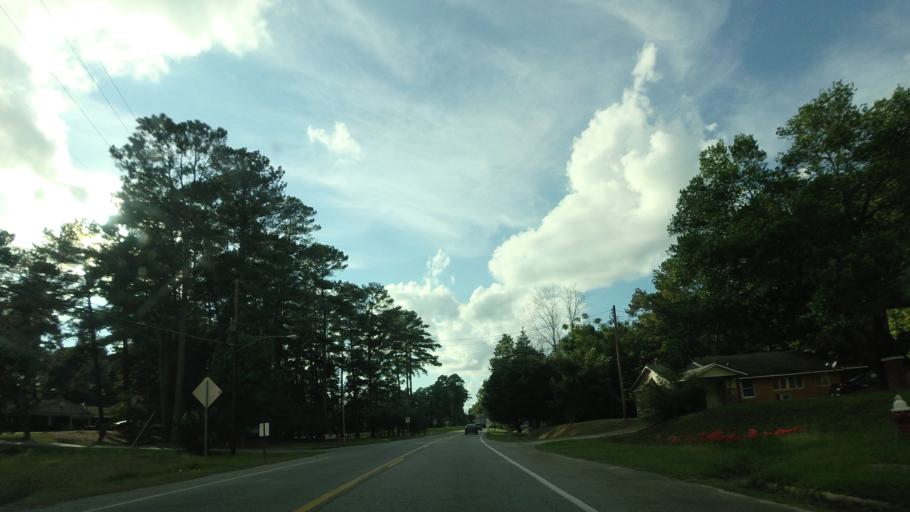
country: US
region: Georgia
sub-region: Pulaski County
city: Hawkinsville
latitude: 32.2856
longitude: -83.4824
